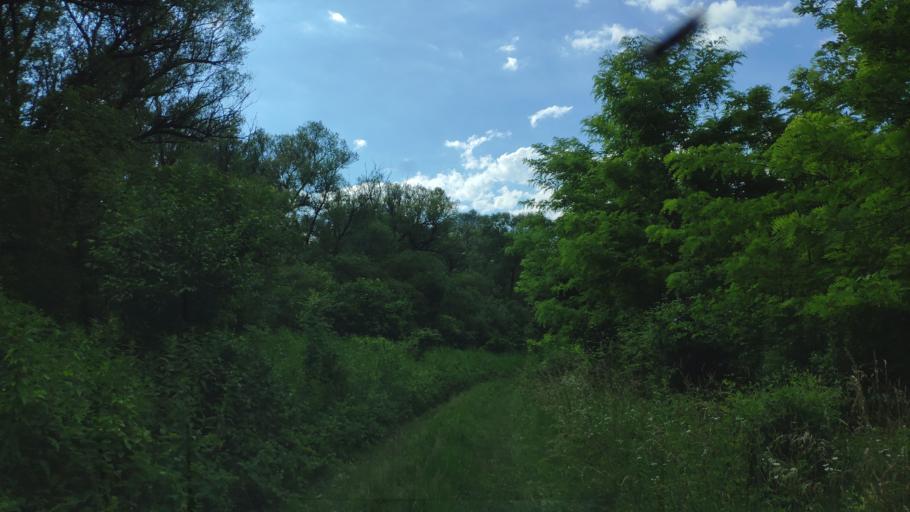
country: SK
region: Banskobystricky
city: Rimavska Sobota
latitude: 48.2570
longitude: 20.1159
